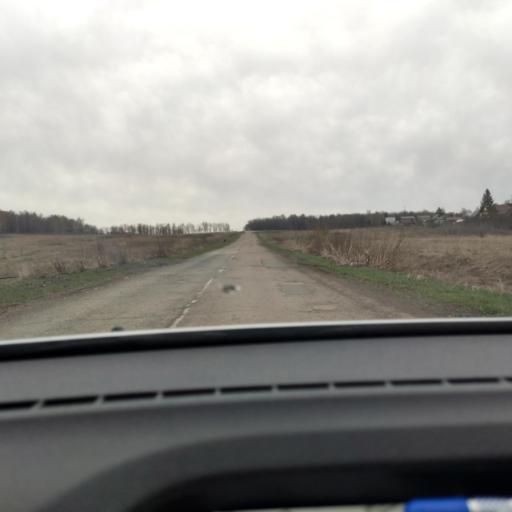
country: RU
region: Bashkortostan
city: Avdon
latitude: 54.6338
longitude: 55.6020
